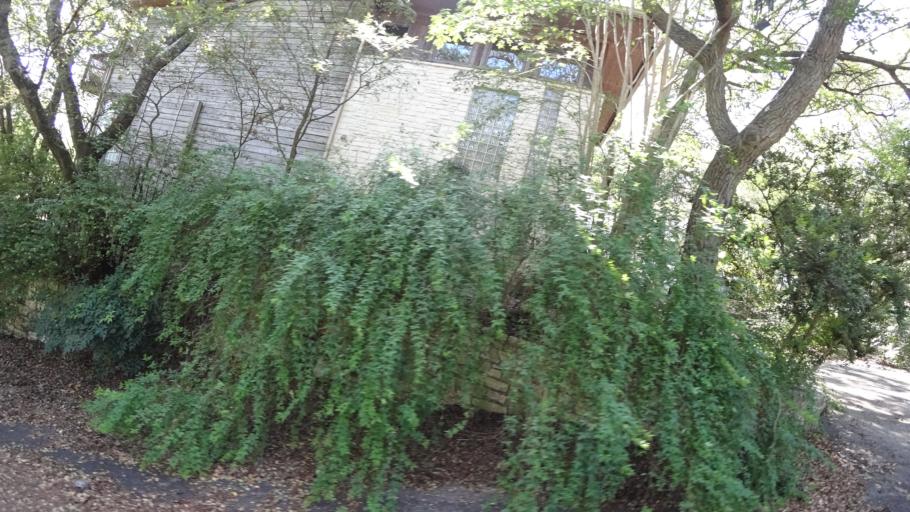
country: US
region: Texas
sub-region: Travis County
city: West Lake Hills
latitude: 30.3014
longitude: -97.7873
